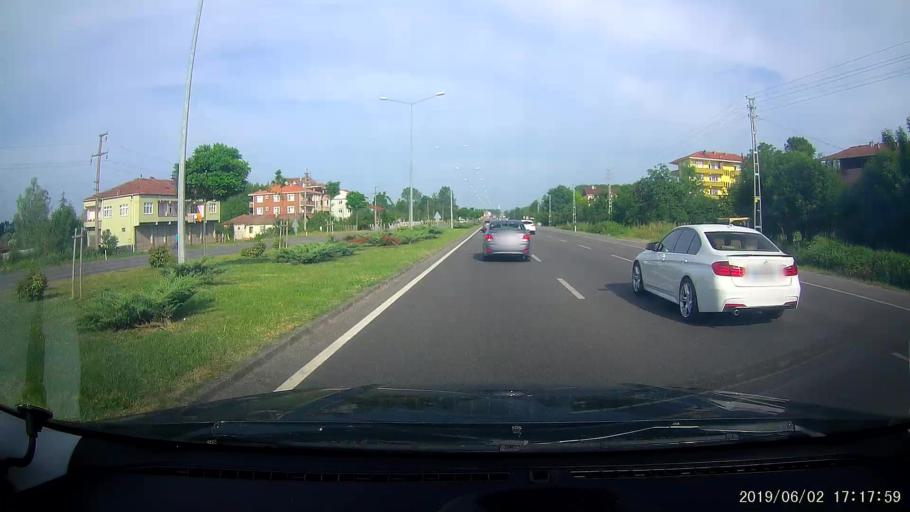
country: TR
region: Samsun
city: Dikbiyik
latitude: 41.2260
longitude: 36.5903
